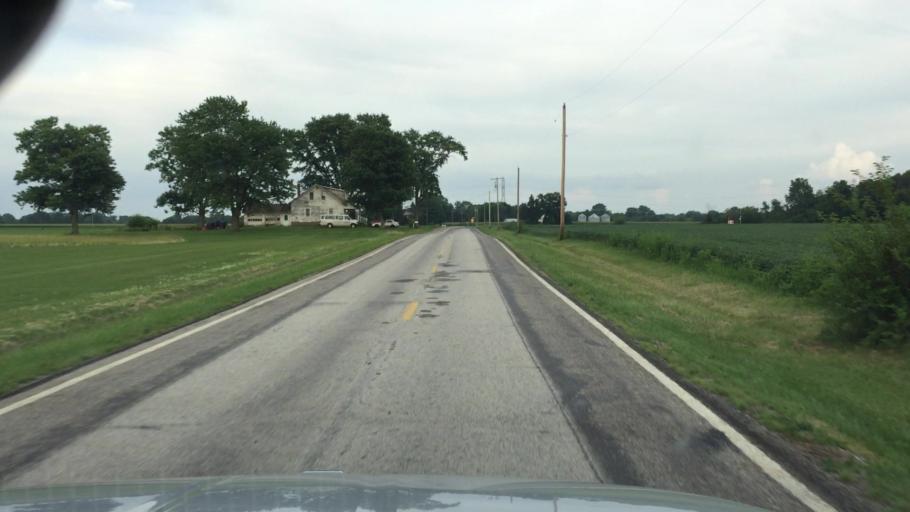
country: US
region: Ohio
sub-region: Franklin County
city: Hilliard
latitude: 40.0750
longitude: -83.2038
